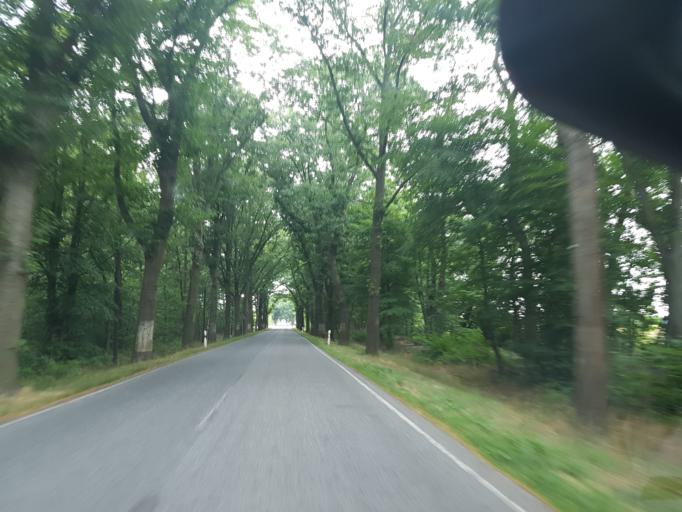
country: DE
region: Brandenburg
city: Dahme
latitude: 51.8450
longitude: 13.4117
